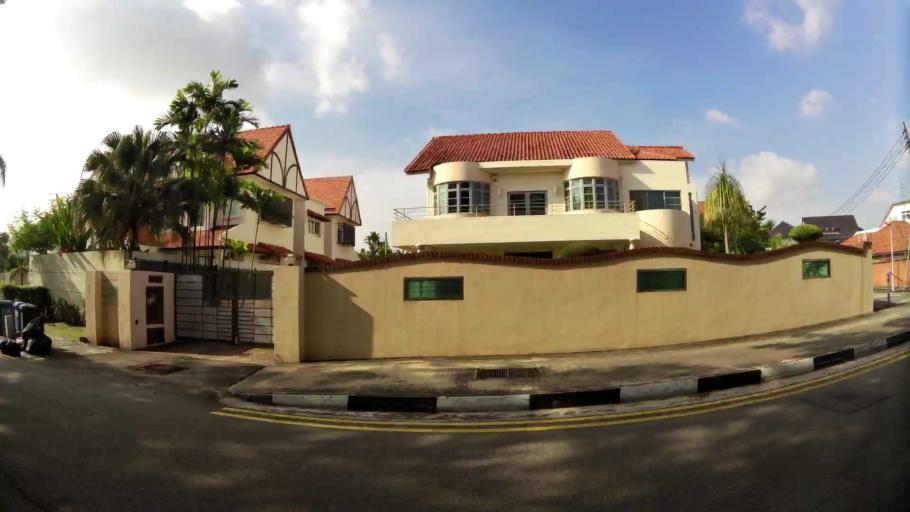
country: SG
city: Singapore
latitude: 1.3165
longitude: 103.9180
